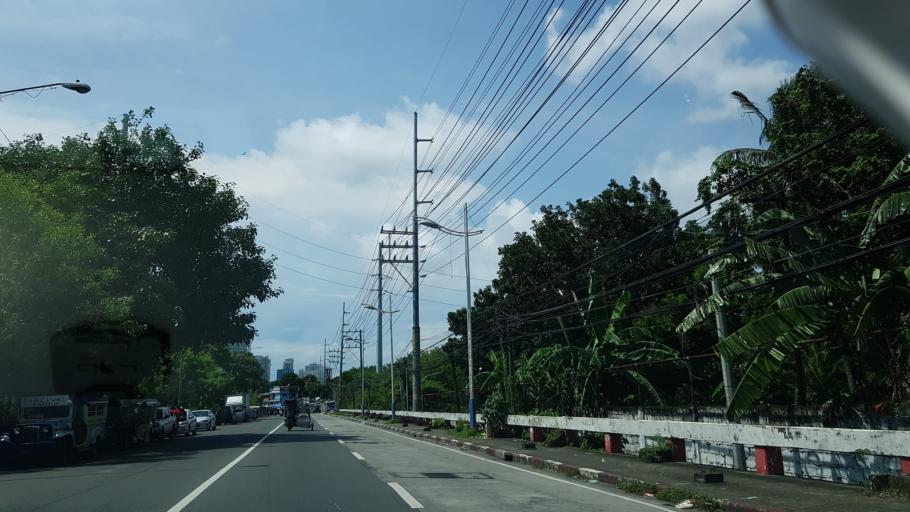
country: PH
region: Metro Manila
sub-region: Makati City
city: Makati City
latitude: 14.5304
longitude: 121.0257
